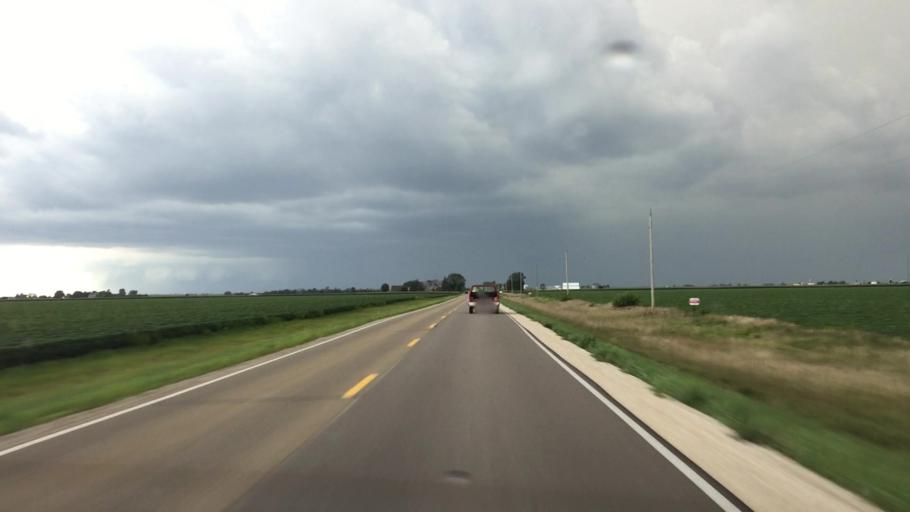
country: US
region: Iowa
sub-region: Henry County
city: New London
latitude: 40.7842
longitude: -91.4845
